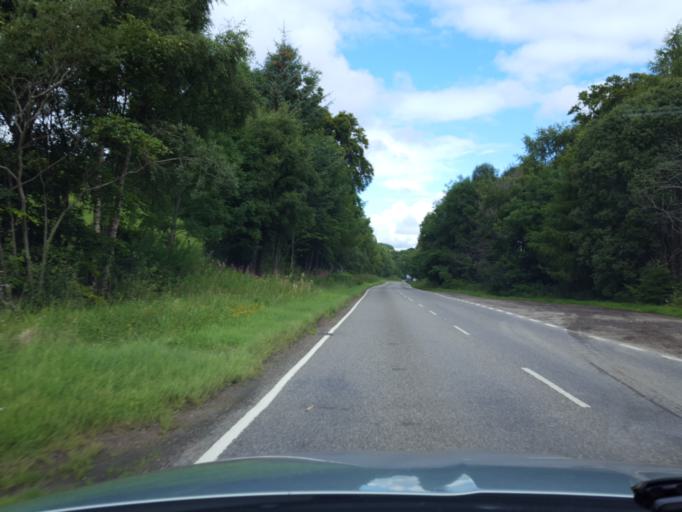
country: GB
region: Scotland
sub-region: Moray
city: Rothes
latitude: 57.5052
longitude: -3.1963
